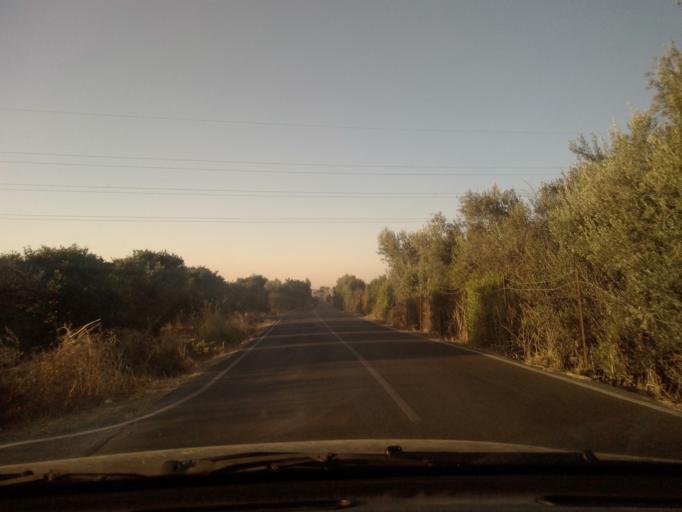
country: CY
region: Limassol
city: Ypsonas
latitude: 34.6659
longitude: 32.9620
